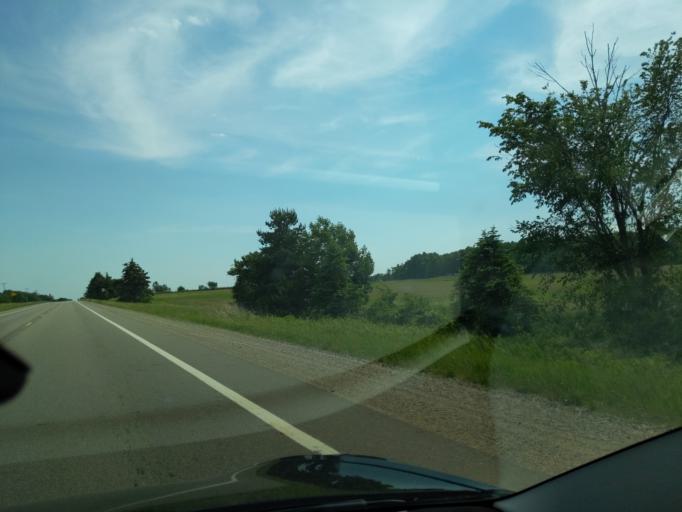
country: US
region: Michigan
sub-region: Barry County
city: Nashville
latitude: 42.6646
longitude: -85.0952
